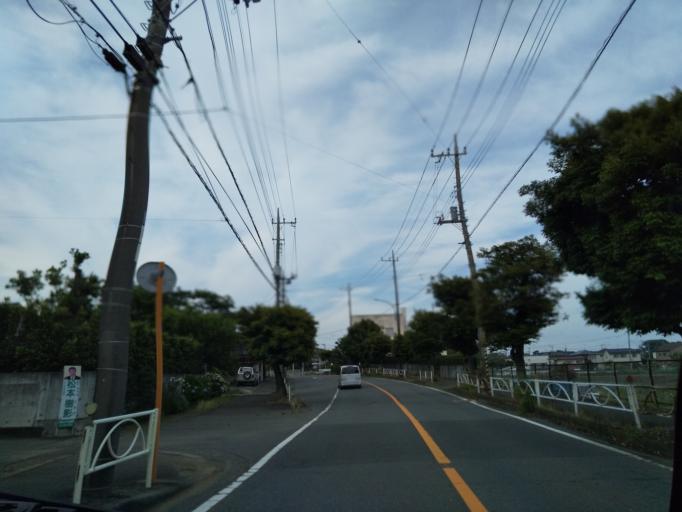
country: JP
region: Kanagawa
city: Atsugi
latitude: 35.4837
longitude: 139.3223
